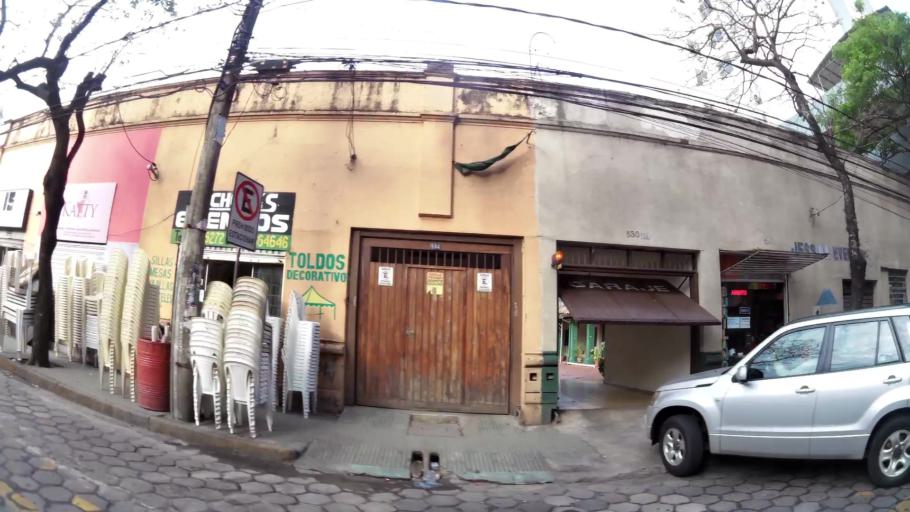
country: BO
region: Santa Cruz
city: Santa Cruz de la Sierra
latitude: -17.7786
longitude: -63.1842
